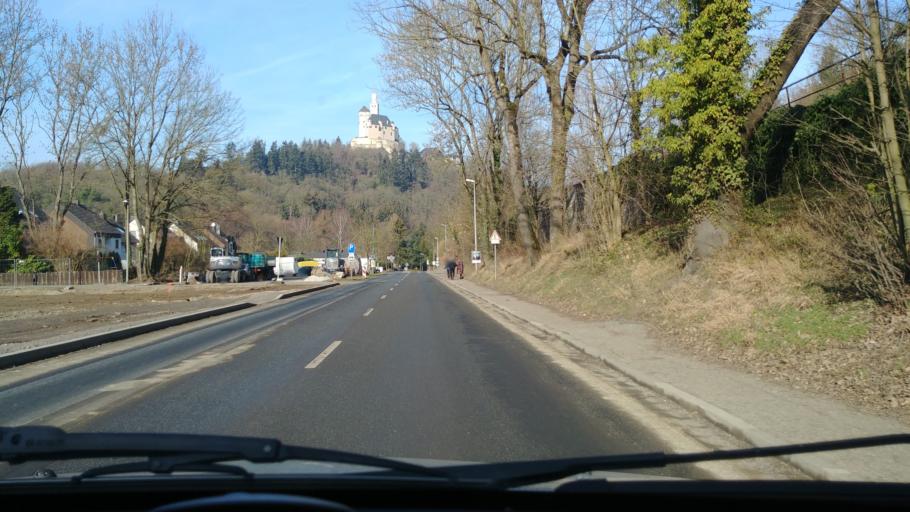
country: DE
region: Rheinland-Pfalz
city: Braubach
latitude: 50.2672
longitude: 7.6549
